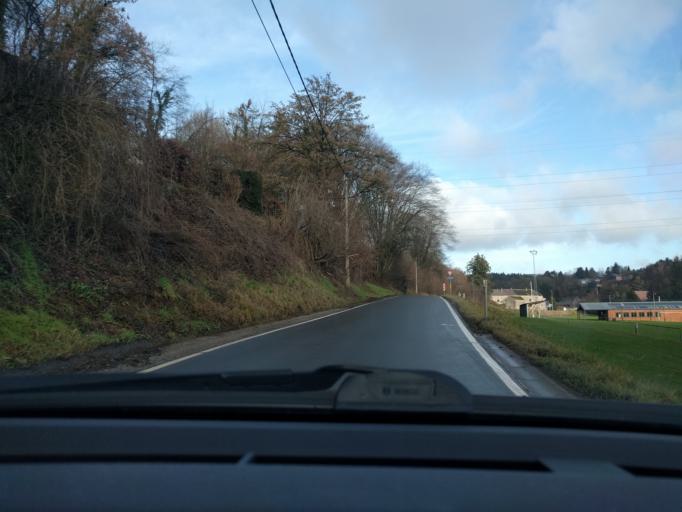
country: BE
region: Wallonia
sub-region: Province de Namur
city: Noville-les-Bois
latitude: 50.5033
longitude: 4.9527
